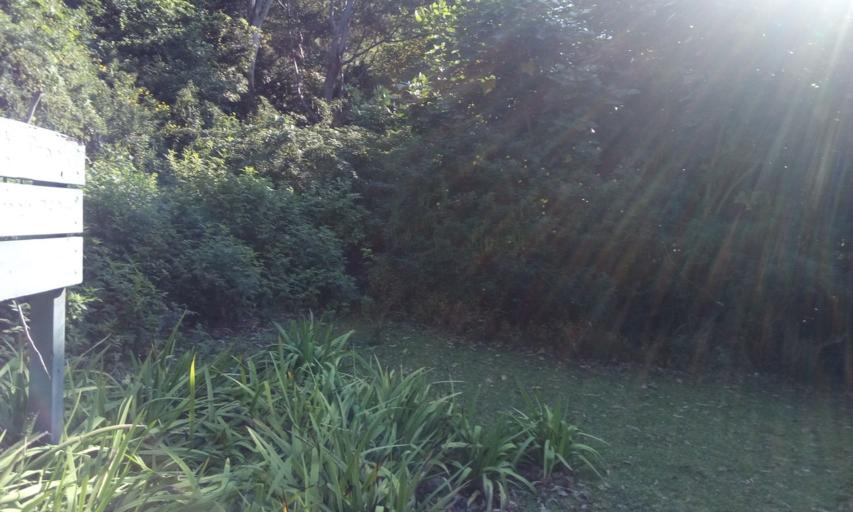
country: AU
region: New South Wales
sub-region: Wollongong
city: Mount Ousley
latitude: -34.3981
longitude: 150.8622
